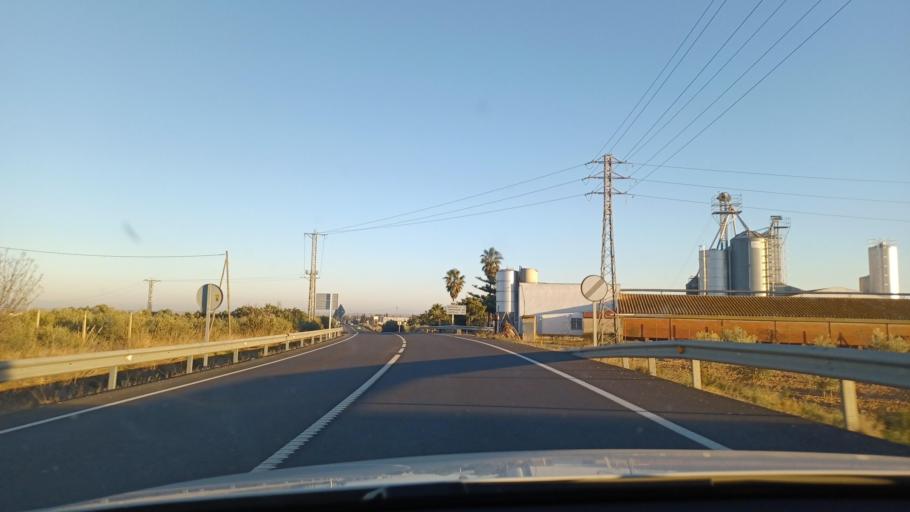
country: ES
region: Catalonia
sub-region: Provincia de Tarragona
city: Amposta
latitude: 40.6995
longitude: 0.5672
